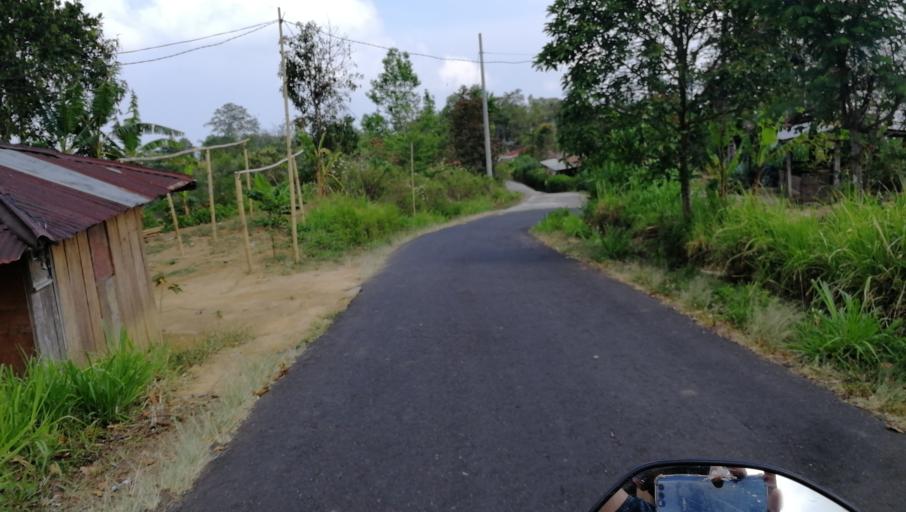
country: ID
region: Bali
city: Banjar Ambengan
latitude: -8.2241
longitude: 115.1510
